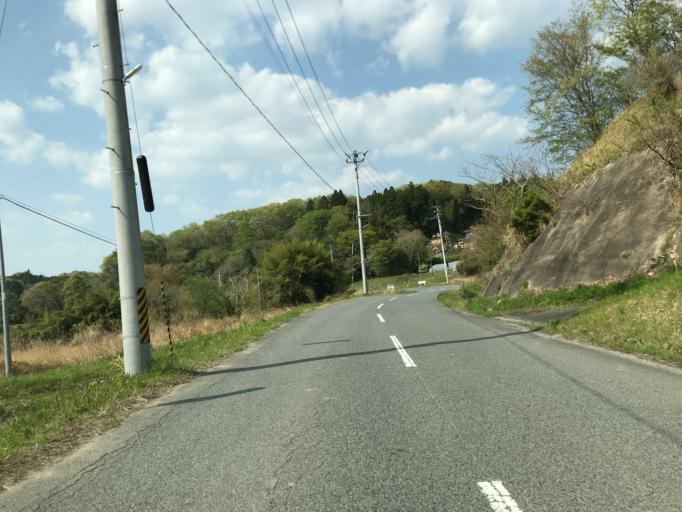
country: JP
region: Fukushima
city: Iwaki
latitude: 36.9728
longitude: 140.7636
